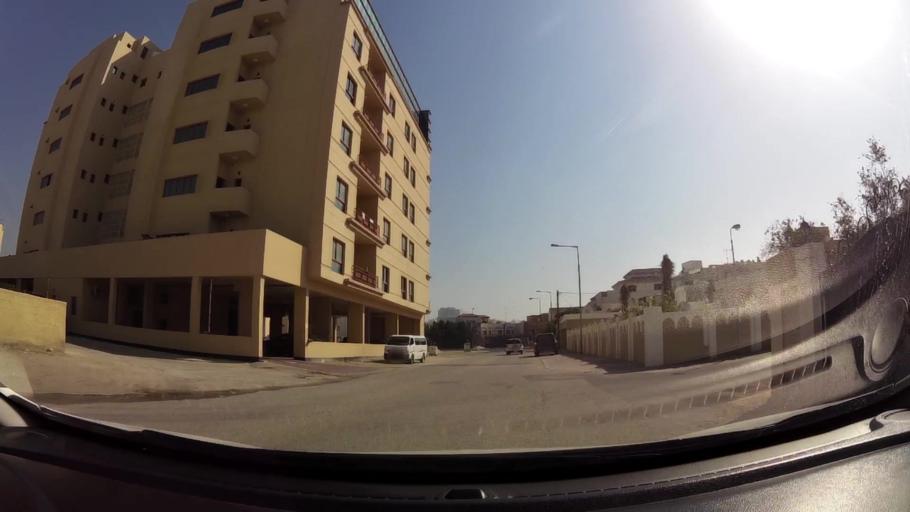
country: BH
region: Manama
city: Manama
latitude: 26.2097
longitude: 50.5886
